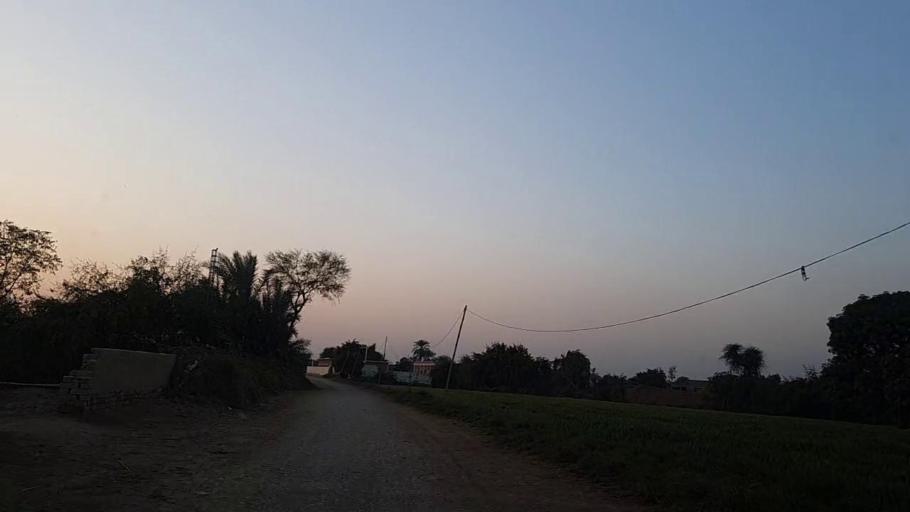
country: PK
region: Sindh
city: Hala
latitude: 25.9375
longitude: 68.4576
